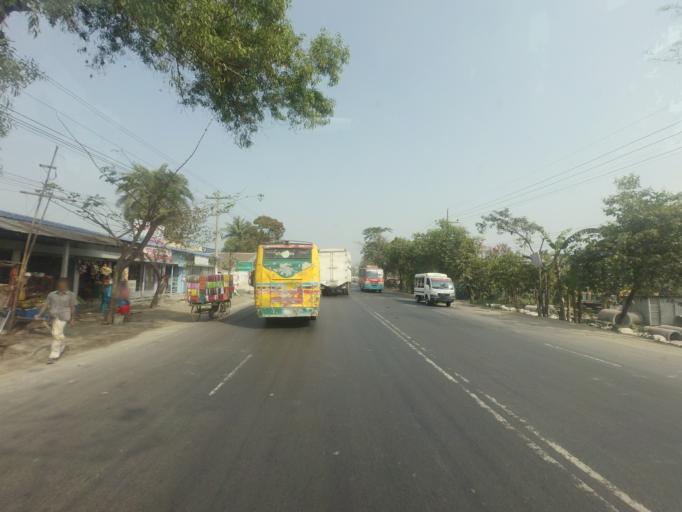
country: BD
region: Dhaka
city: Narsingdi
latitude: 23.8754
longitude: 90.6669
